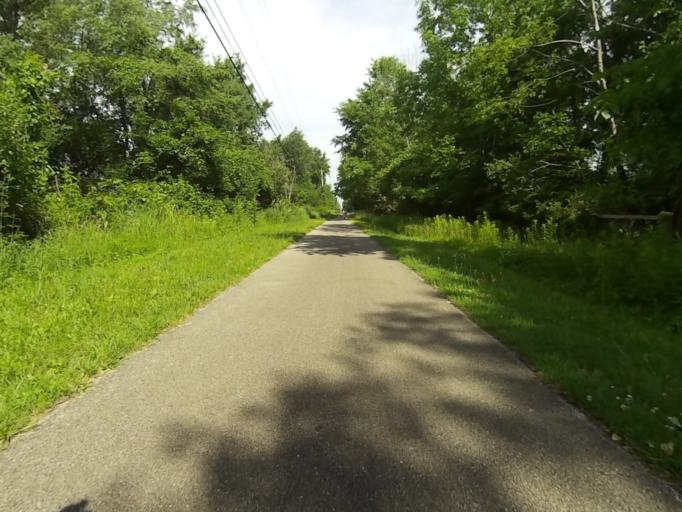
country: US
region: Ohio
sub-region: Summit County
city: Hudson
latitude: 41.2202
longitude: -81.4747
